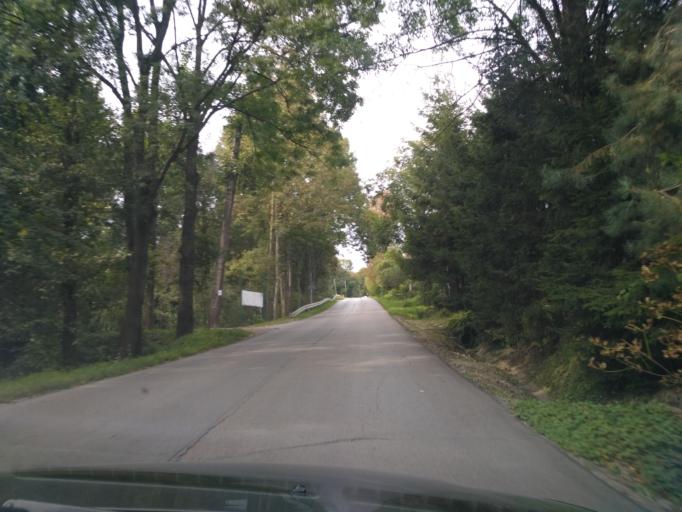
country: PL
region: Subcarpathian Voivodeship
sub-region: Powiat rzeszowski
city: Trzciana
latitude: 50.0462
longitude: 21.8328
